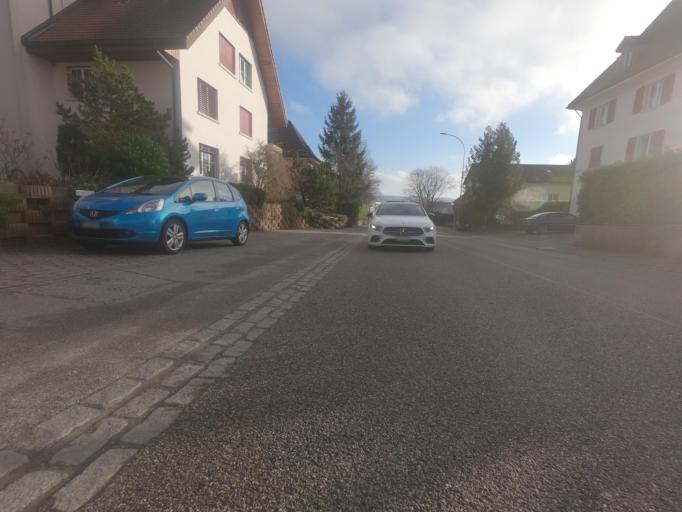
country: CH
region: Solothurn
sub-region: Bezirk Lebern
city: Bettlach
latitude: 47.2012
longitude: 7.4251
